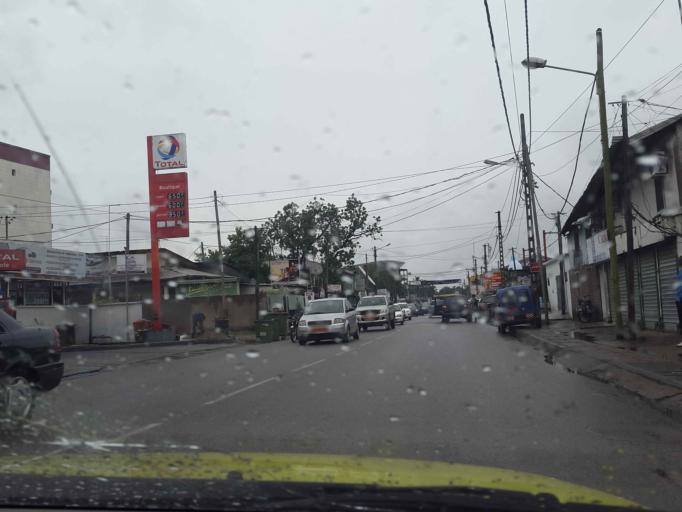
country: CM
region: Littoral
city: Douala
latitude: 4.0359
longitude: 9.6946
